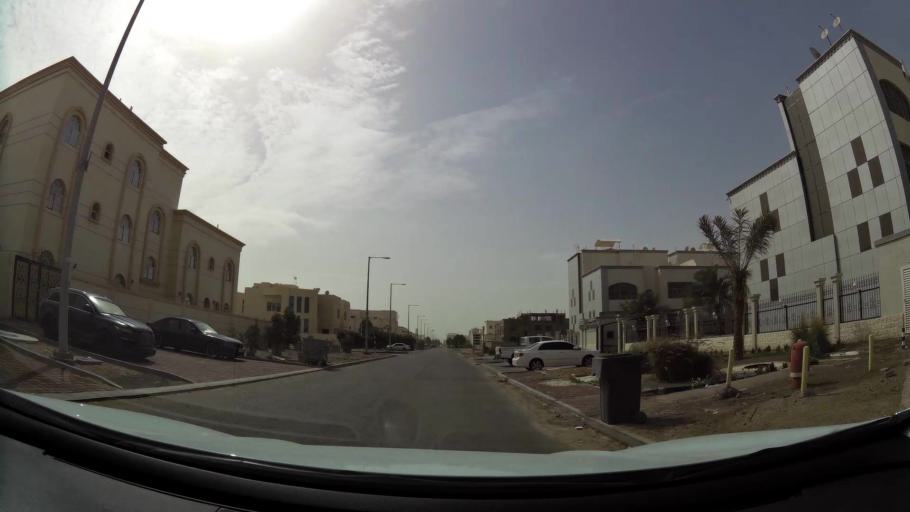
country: AE
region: Abu Dhabi
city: Abu Dhabi
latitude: 24.4107
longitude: 54.5627
